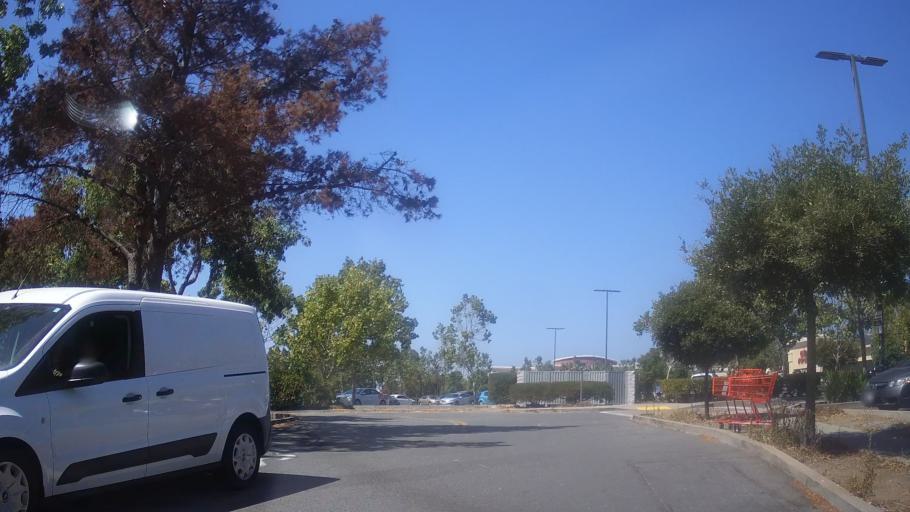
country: US
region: California
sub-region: Alameda County
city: Albany
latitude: 37.8981
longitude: -122.3005
